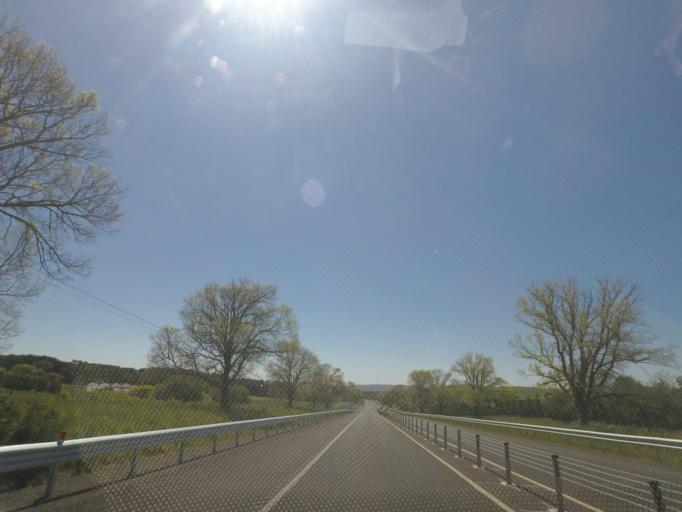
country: AU
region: Victoria
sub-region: Hume
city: Sunbury
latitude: -37.3164
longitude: 144.7403
